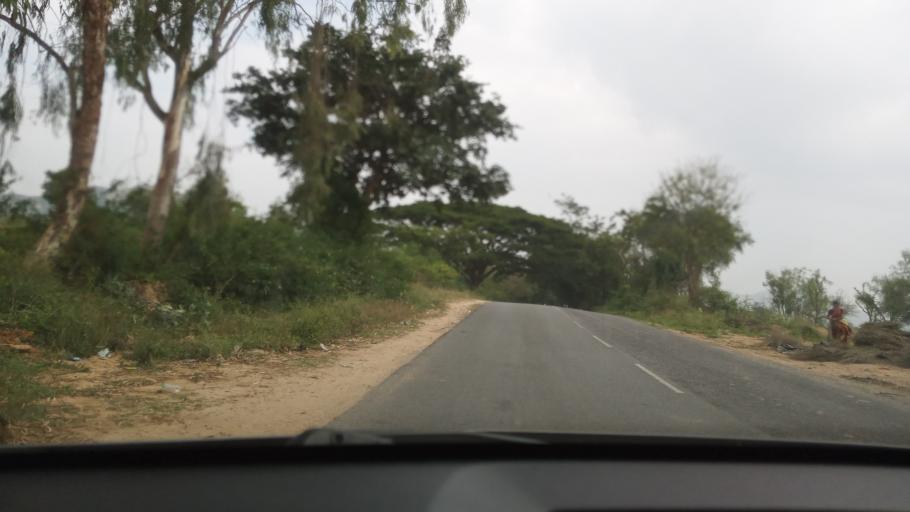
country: IN
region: Andhra Pradesh
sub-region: Chittoor
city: Pakala
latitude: 13.6563
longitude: 78.8441
